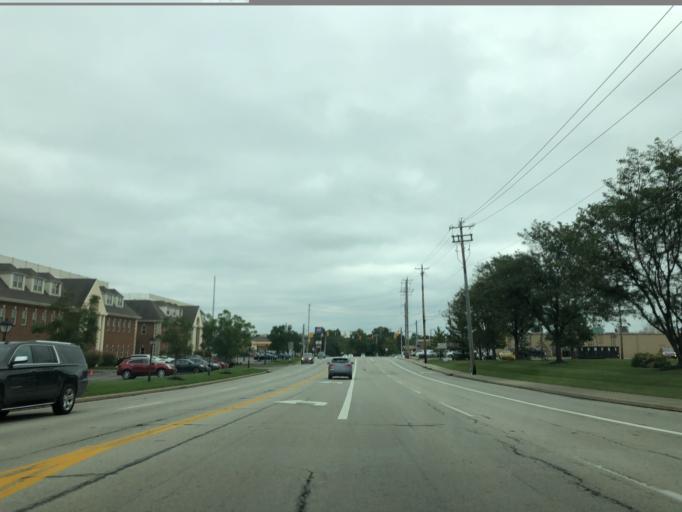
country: US
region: Ohio
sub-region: Hamilton County
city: Sixteen Mile Stand
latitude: 39.2735
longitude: -84.3291
